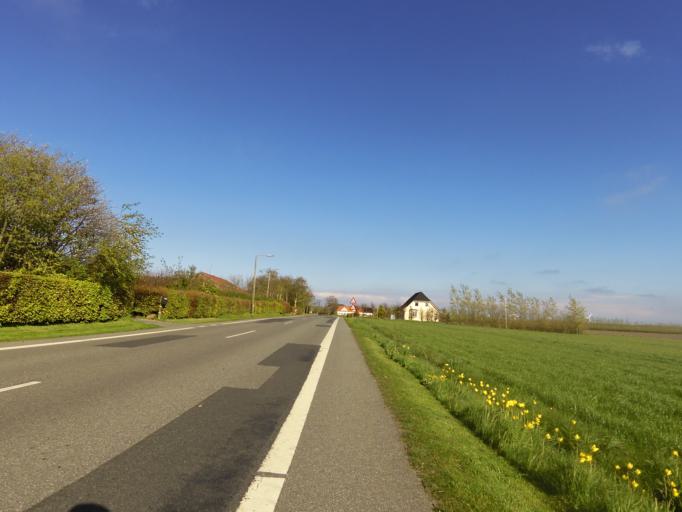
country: DK
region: South Denmark
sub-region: Tonder Kommune
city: Sherrebek
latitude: 55.1560
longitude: 8.8243
